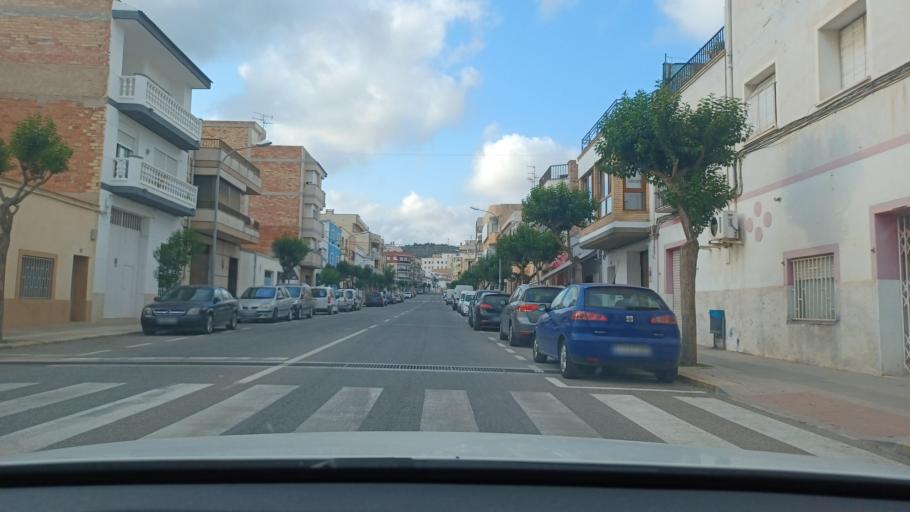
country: ES
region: Catalonia
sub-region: Provincia de Tarragona
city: Alcanar
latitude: 40.5414
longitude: 0.4776
